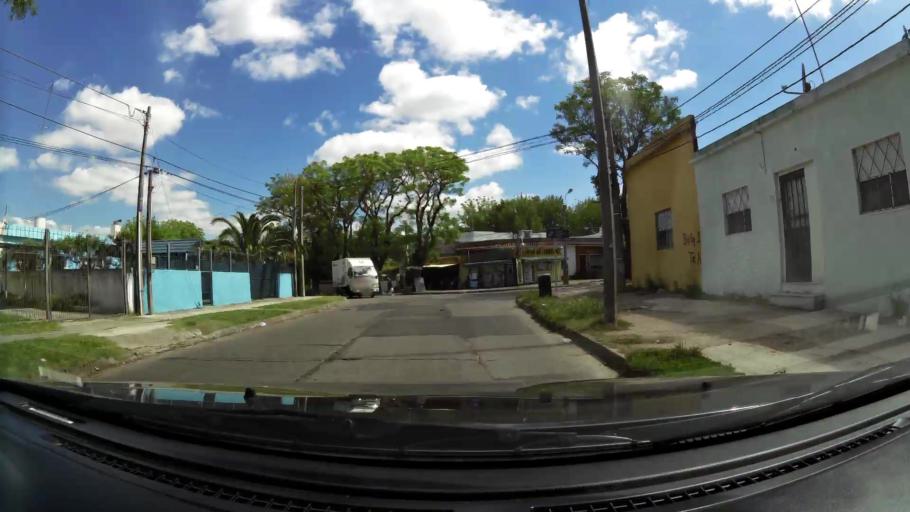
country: UY
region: Montevideo
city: Montevideo
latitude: -34.8537
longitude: -56.1444
